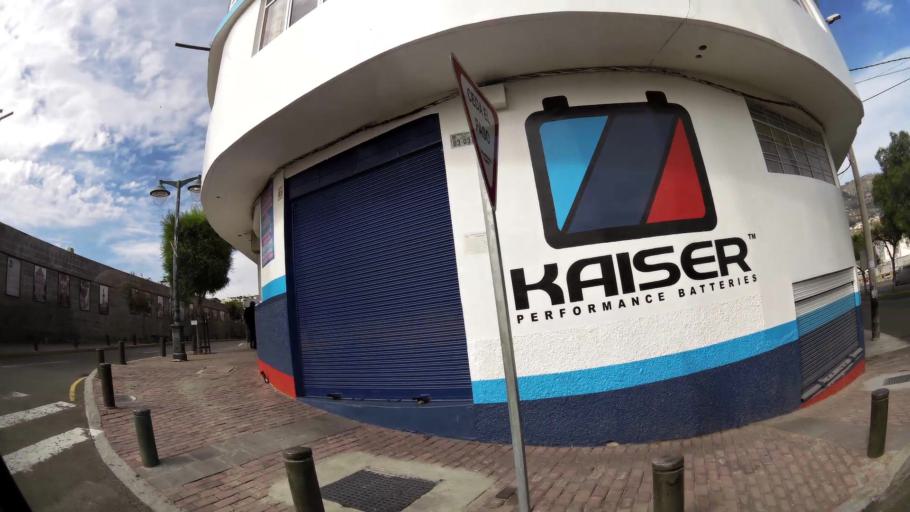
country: EC
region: Tungurahua
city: Ambato
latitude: -1.2313
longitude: -78.6200
